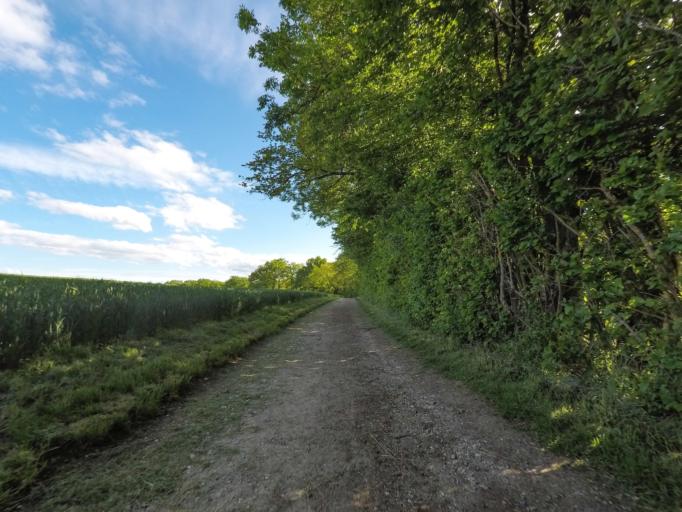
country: FR
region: Rhone-Alpes
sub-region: Departement de l'Ain
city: Chevry
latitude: 46.2713
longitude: 6.0637
